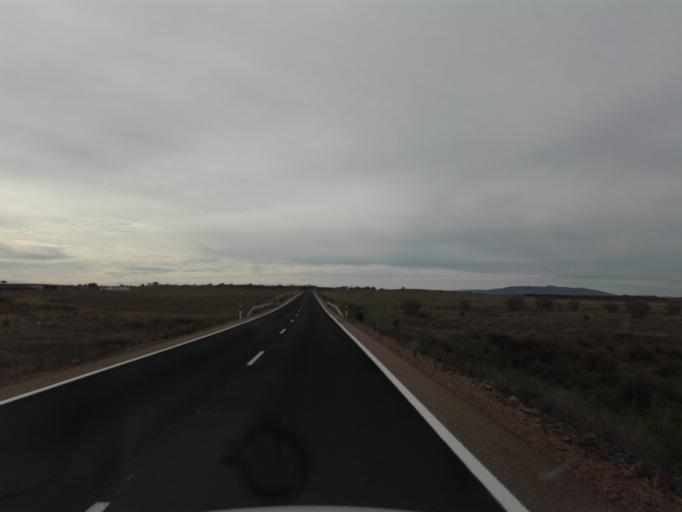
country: ES
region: Extremadura
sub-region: Provincia de Badajoz
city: Valencia de las Torres
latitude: 38.3306
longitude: -5.9643
